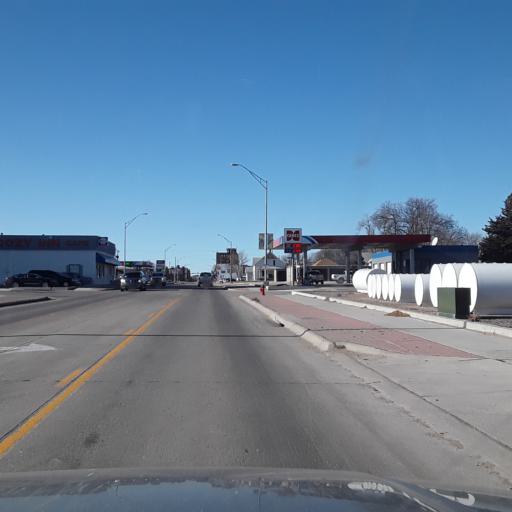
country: US
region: Nebraska
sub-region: Phelps County
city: Holdrege
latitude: 40.4381
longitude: -99.3636
